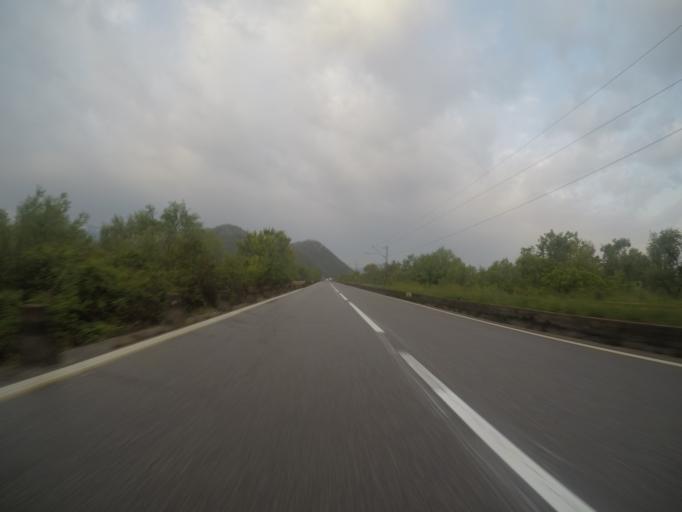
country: ME
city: Mojanovici
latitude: 42.2894
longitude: 19.1497
